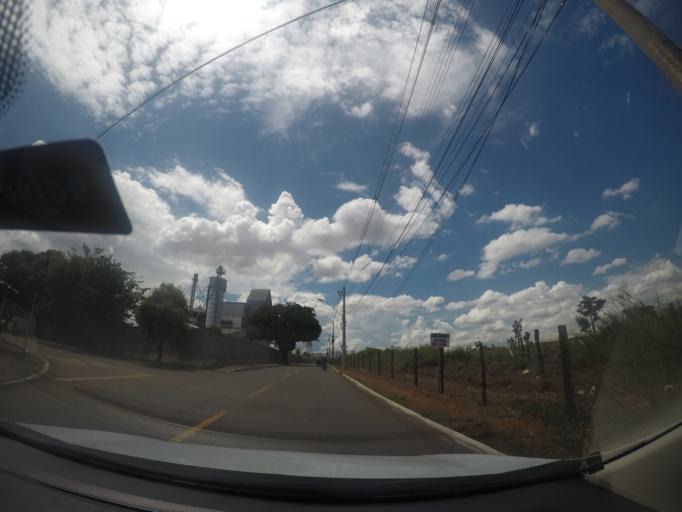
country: BR
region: Goias
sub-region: Goiania
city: Goiania
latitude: -16.7021
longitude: -49.3447
